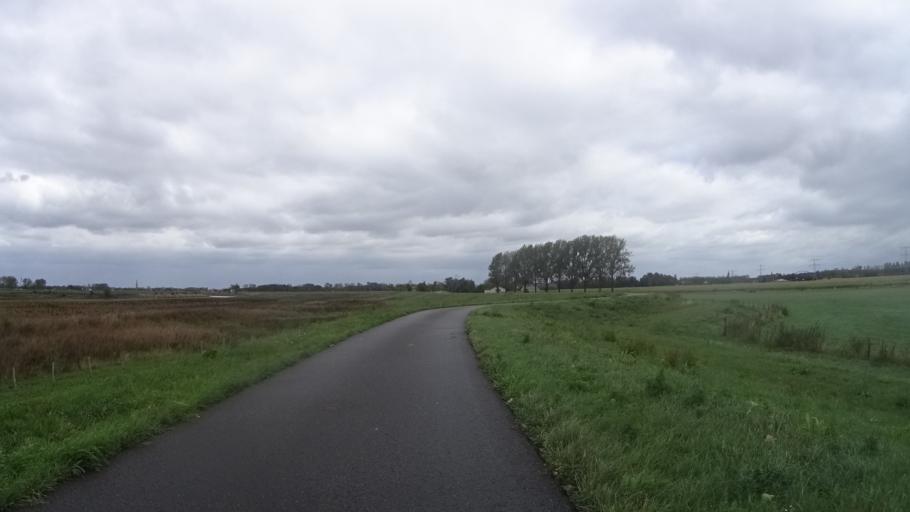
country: BE
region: Flanders
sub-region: Provincie Limburg
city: Maaseik
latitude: 51.0703
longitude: 5.8066
